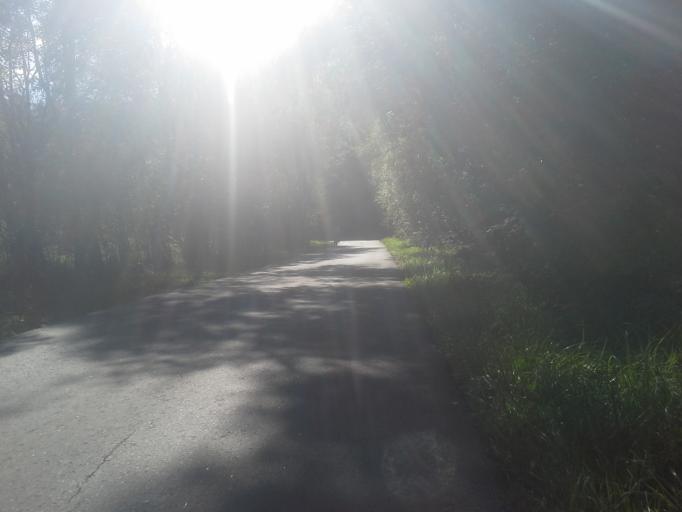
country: RU
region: Moskovskaya
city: Kievskij
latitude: 55.3330
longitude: 36.9940
